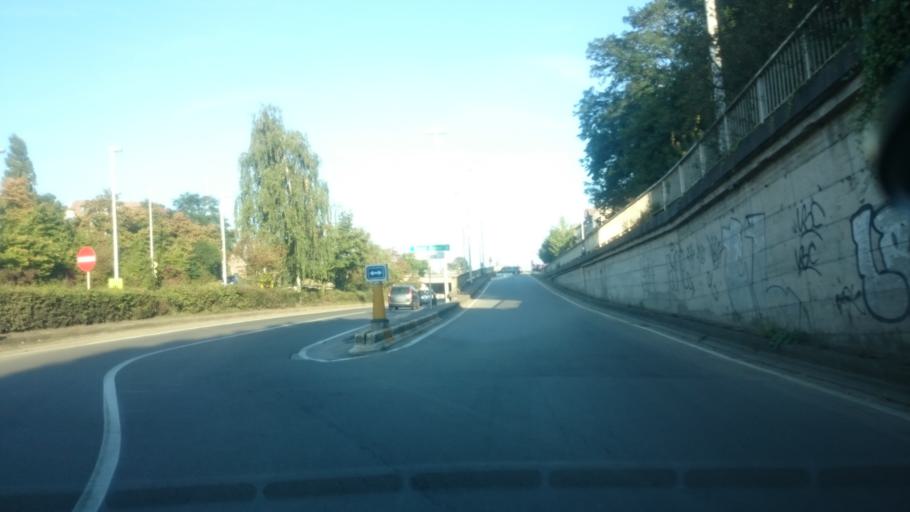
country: BE
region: Brussels Capital
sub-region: Bruxelles-Capitale
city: Brussels
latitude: 50.8151
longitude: 4.4052
